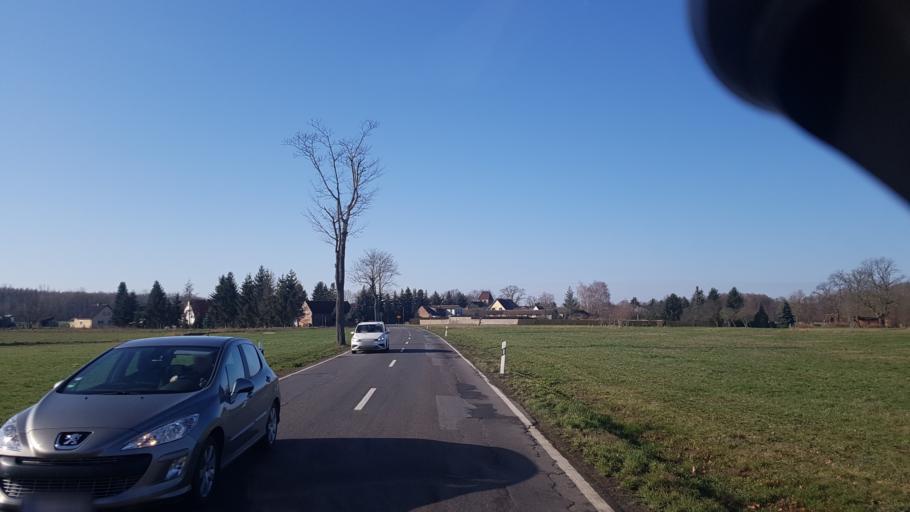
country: DE
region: Brandenburg
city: Luebben
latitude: 51.8493
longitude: 13.8328
